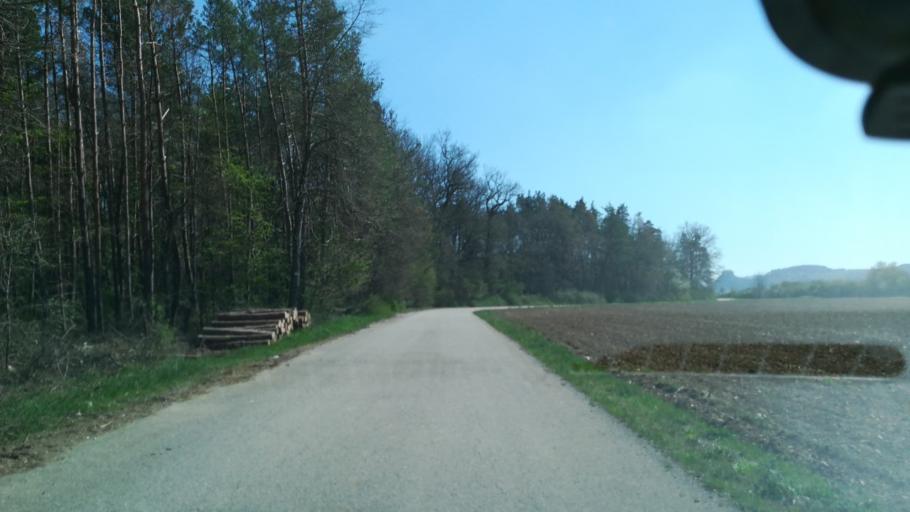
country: DE
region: Baden-Wuerttemberg
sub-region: Freiburg Region
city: Muhlhausen-Ehingen
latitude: 47.8404
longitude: 8.8175
